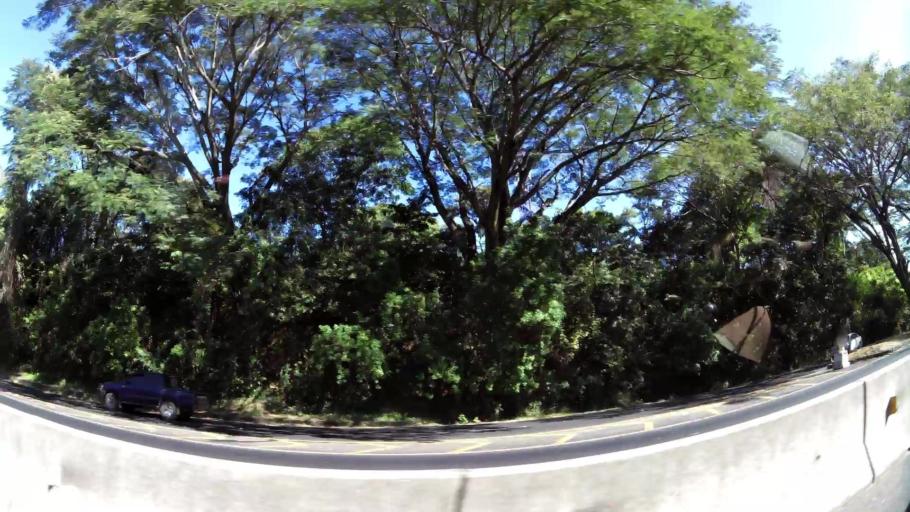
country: SV
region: Santa Ana
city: Santa Ana
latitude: 13.9553
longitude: -89.5700
